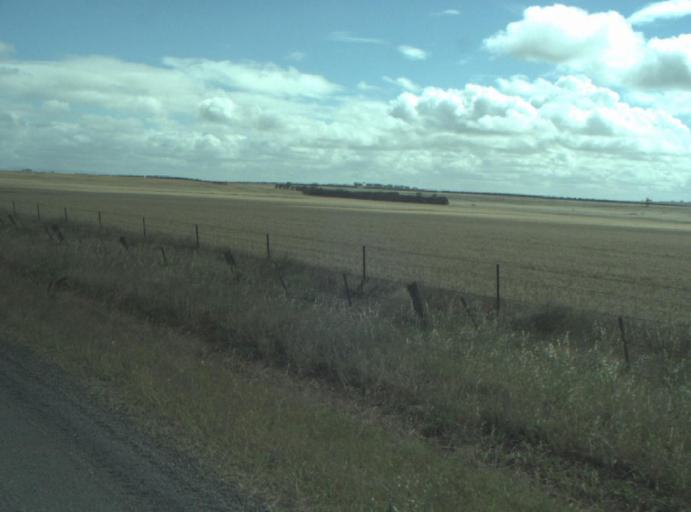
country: AU
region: Victoria
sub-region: Greater Geelong
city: Lara
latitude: -37.9125
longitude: 144.3152
